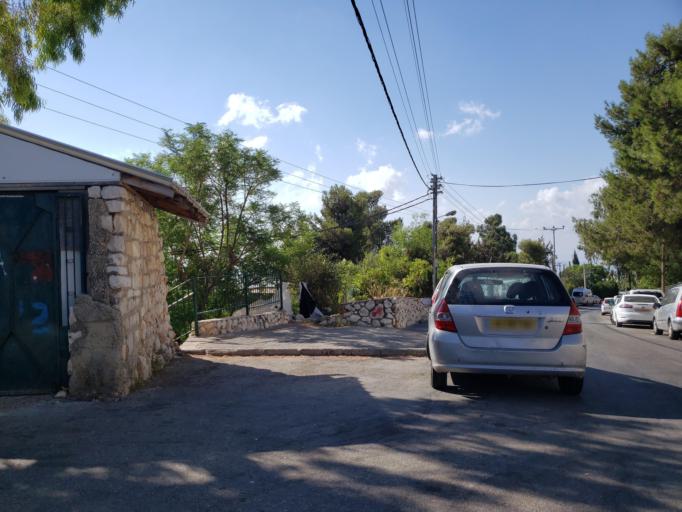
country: IL
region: Northern District
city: Safed
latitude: 32.9579
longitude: 35.5004
